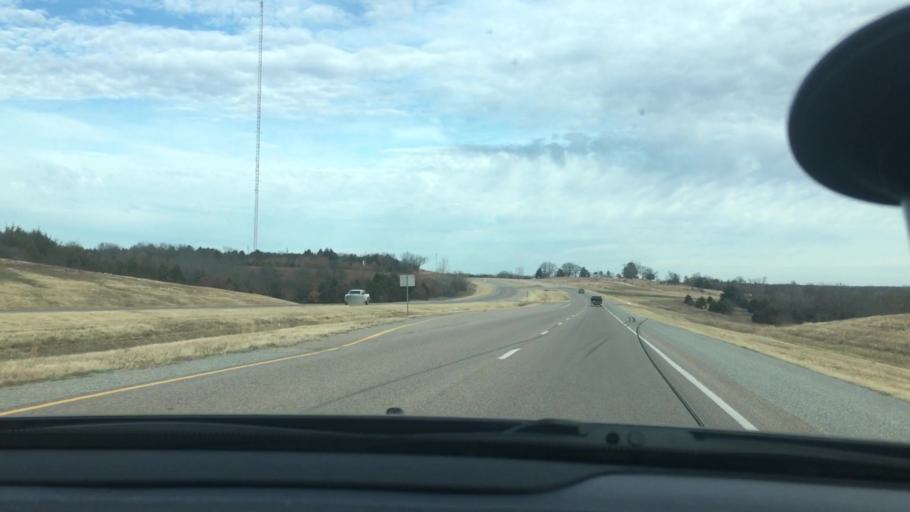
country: US
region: Oklahoma
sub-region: Pontotoc County
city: Byng
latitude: 34.8956
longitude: -96.6749
